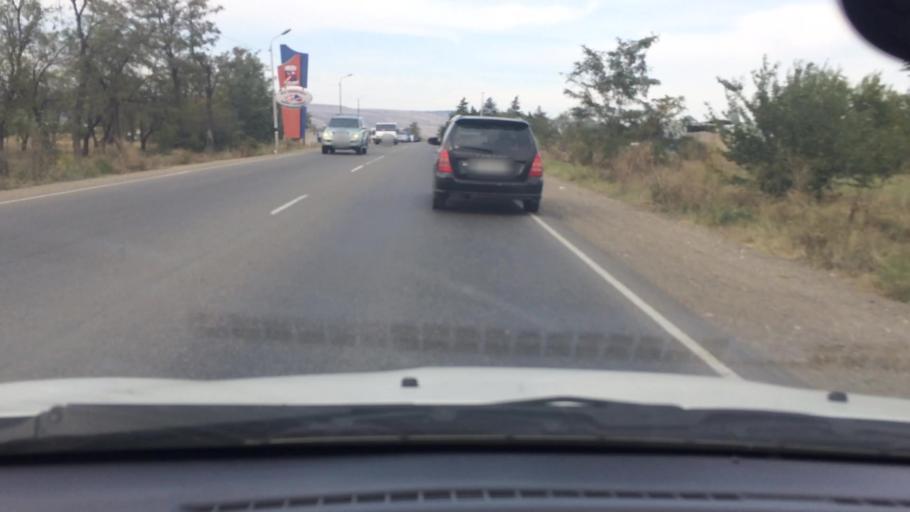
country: GE
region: T'bilisi
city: Tbilisi
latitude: 41.5899
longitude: 44.7800
